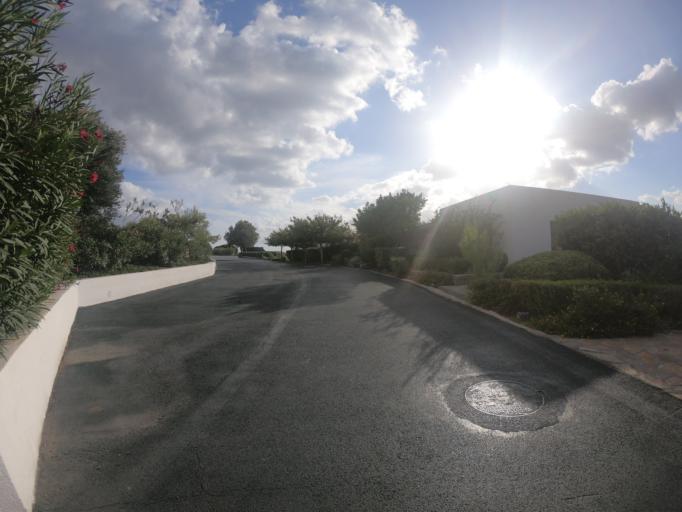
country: GR
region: Attica
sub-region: Nomarchia Anatolikis Attikis
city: Saronida
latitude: 37.7756
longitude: 23.8861
